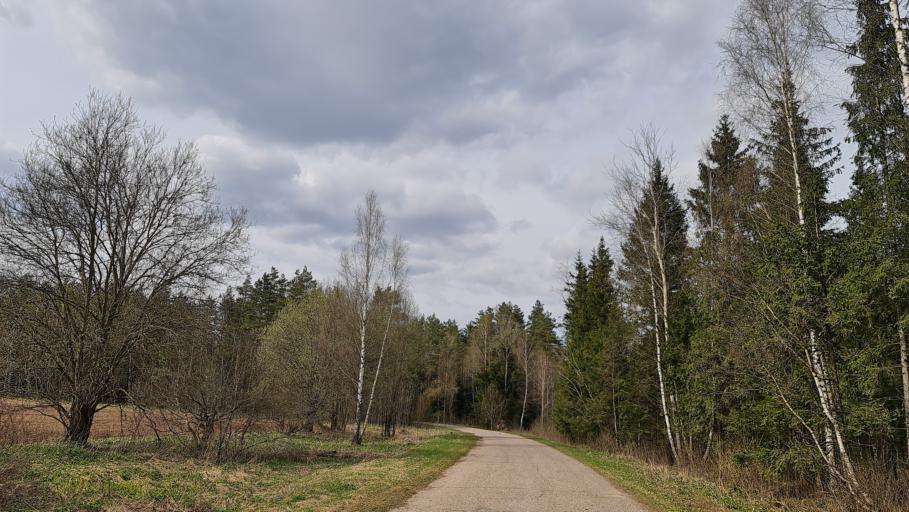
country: BY
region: Vitebsk
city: Byahoml'
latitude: 54.7478
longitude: 28.0411
